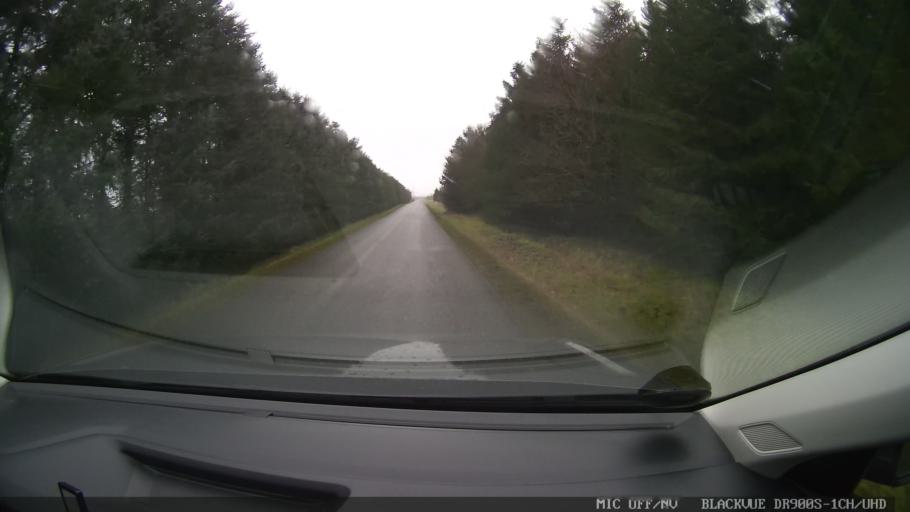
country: DK
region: Central Jutland
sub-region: Viborg Kommune
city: Karup
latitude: 56.2422
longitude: 9.1430
